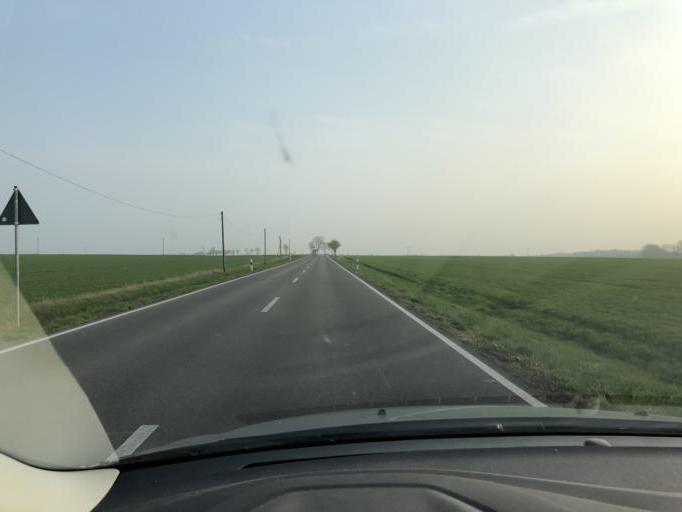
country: DE
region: Saxony
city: Zschortau
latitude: 51.4615
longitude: 12.3509
